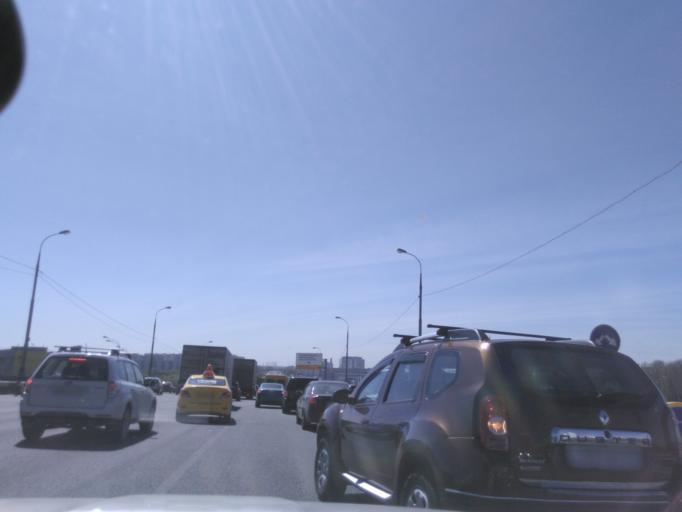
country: RU
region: Moscow
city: Strogino
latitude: 55.8333
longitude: 37.3954
